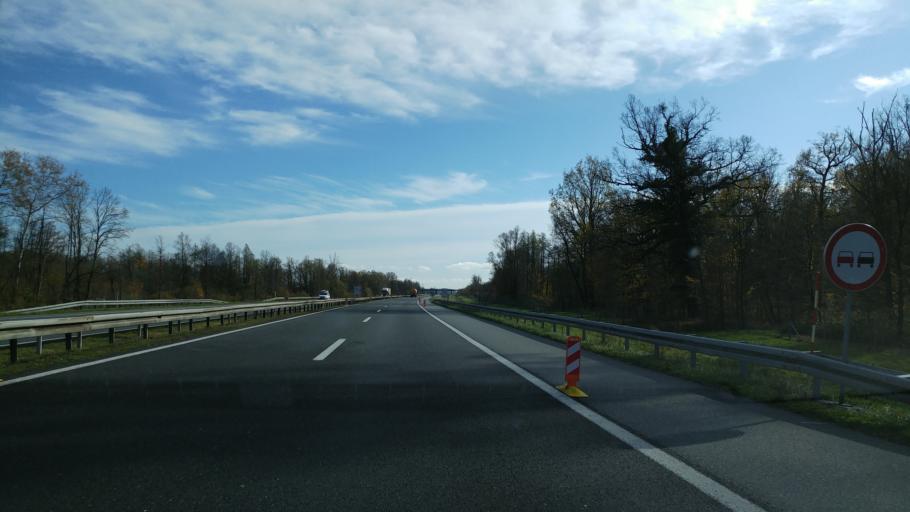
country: HR
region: Sisacko-Moslavacka
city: Husain
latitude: 45.4389
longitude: 16.8252
